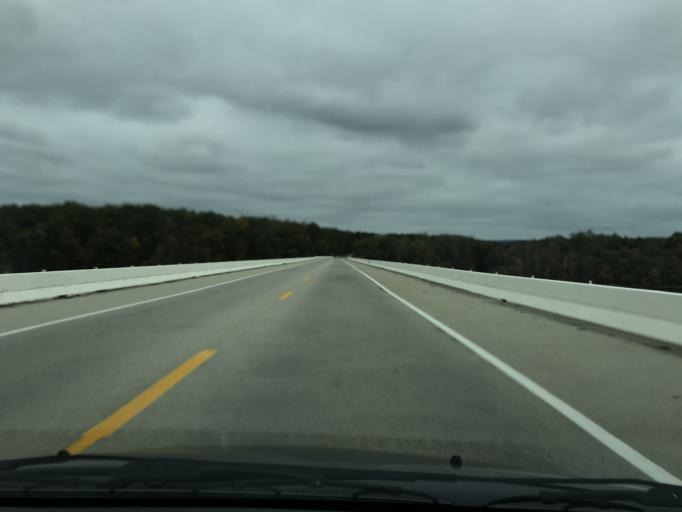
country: US
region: Tennessee
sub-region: Rhea County
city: Graysville
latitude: 35.4106
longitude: -85.0197
